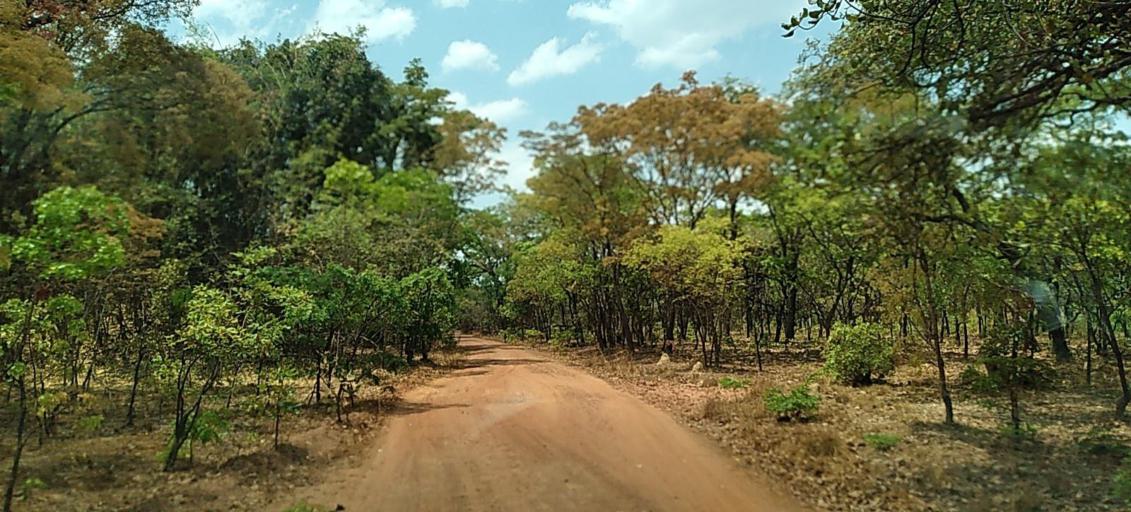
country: ZM
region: Copperbelt
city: Chililabombwe
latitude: -12.5072
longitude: 27.6337
